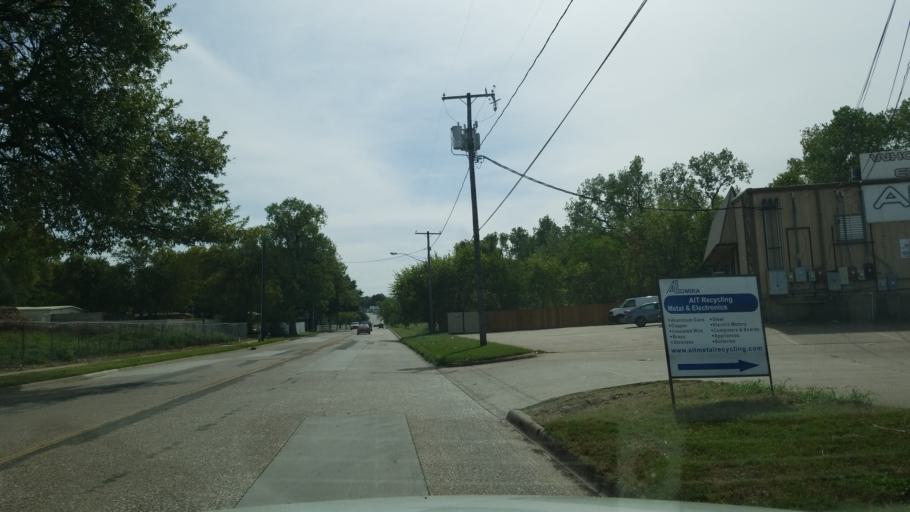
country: US
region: Texas
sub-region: Dallas County
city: Highland Park
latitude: 32.7899
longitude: -96.7251
